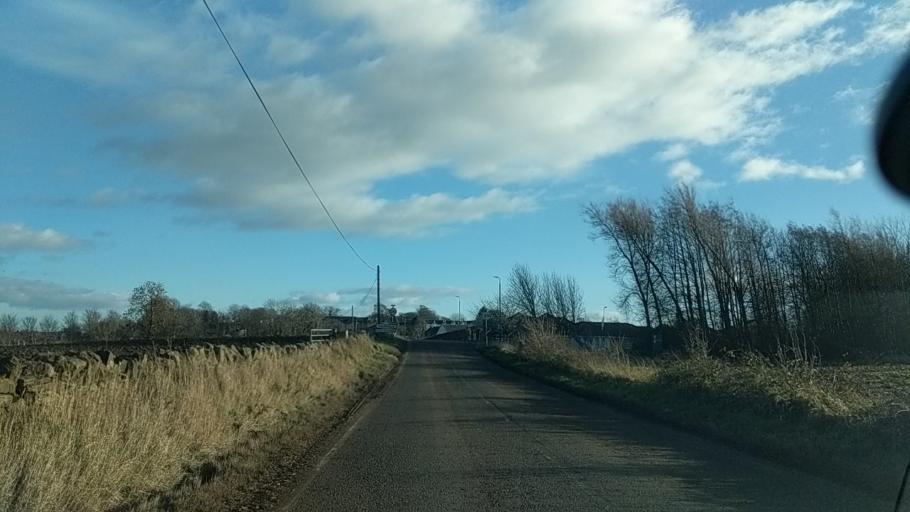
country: GB
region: Scotland
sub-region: West Lothian
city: Linlithgow
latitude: 55.9772
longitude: -3.5326
